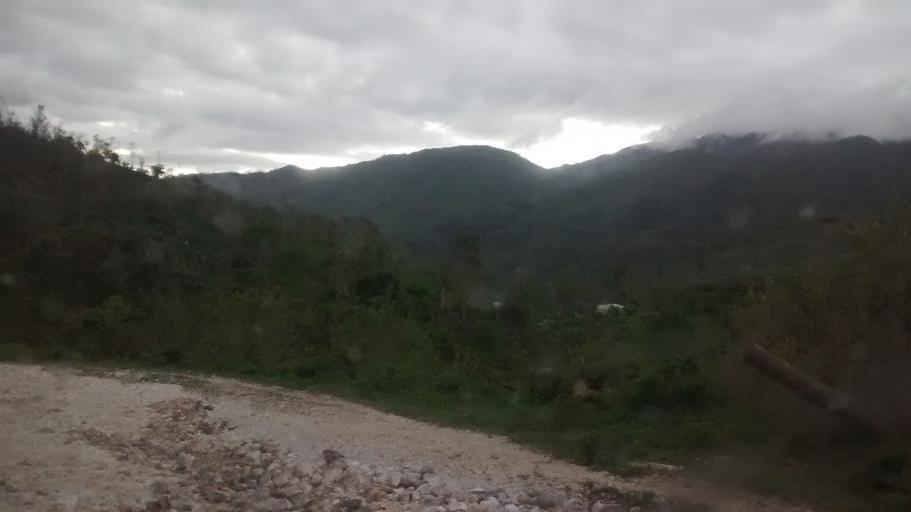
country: HT
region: Grandans
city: Corail
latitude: 18.4771
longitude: -73.7929
